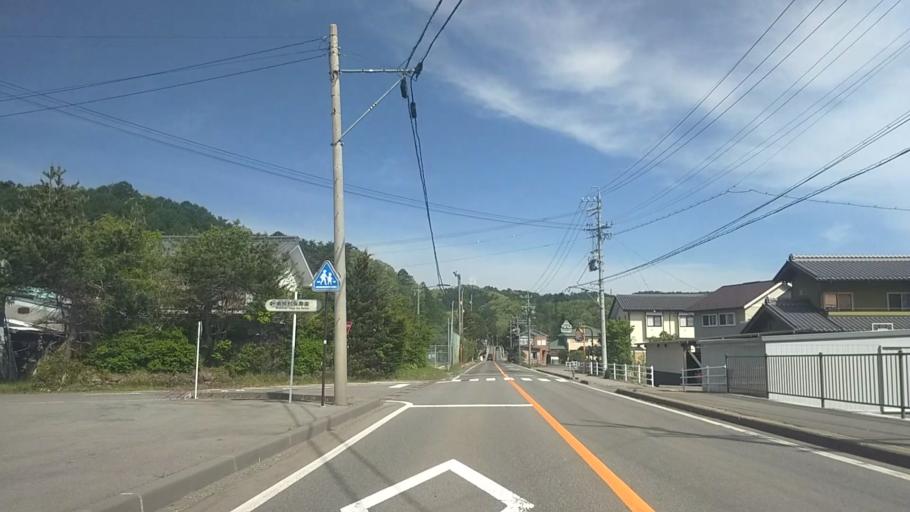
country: JP
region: Nagano
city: Saku
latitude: 36.0359
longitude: 138.4763
